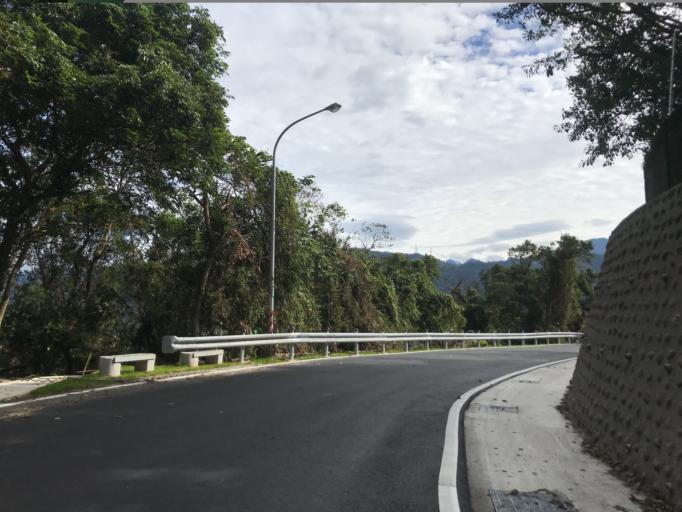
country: TW
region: Taiwan
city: Daxi
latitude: 24.8396
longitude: 121.2445
